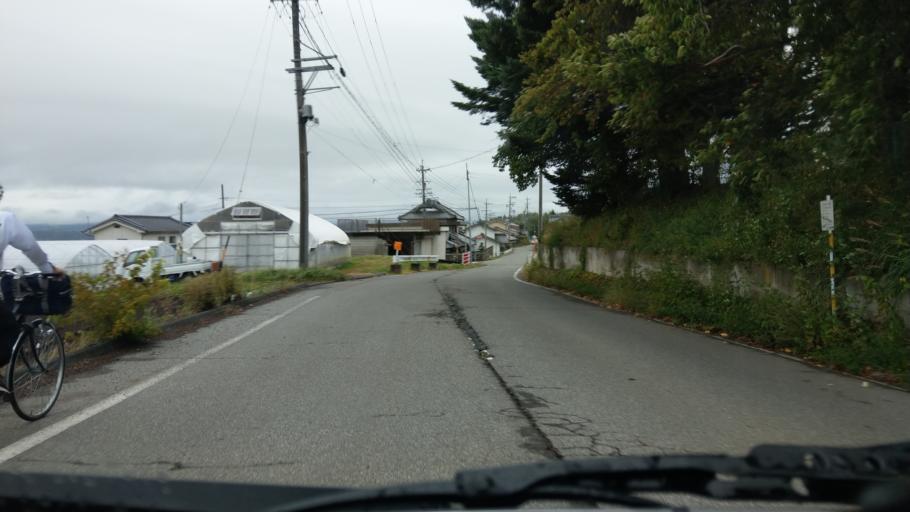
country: JP
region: Nagano
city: Komoro
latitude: 36.3332
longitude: 138.4555
